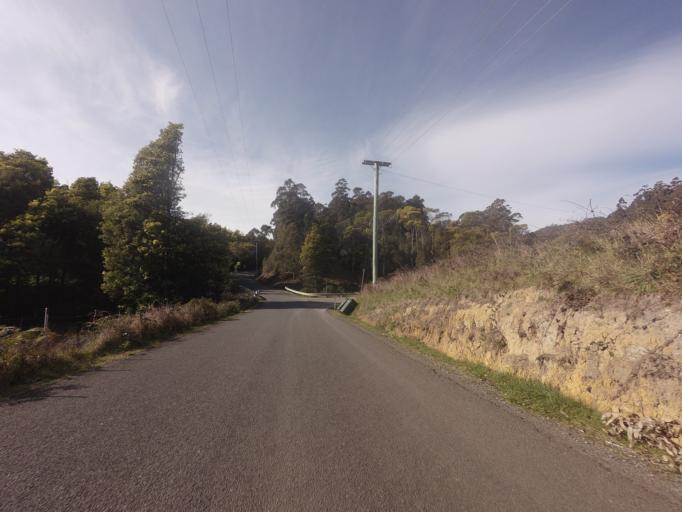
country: AU
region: Tasmania
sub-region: Huon Valley
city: Cygnet
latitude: -43.1747
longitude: 147.1563
